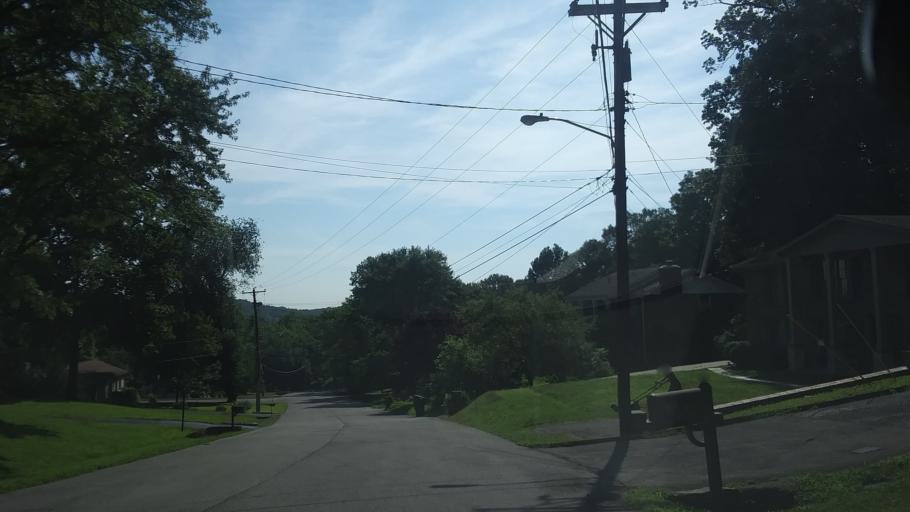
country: US
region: Tennessee
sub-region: Davidson County
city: Belle Meade
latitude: 36.0790
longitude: -86.8916
